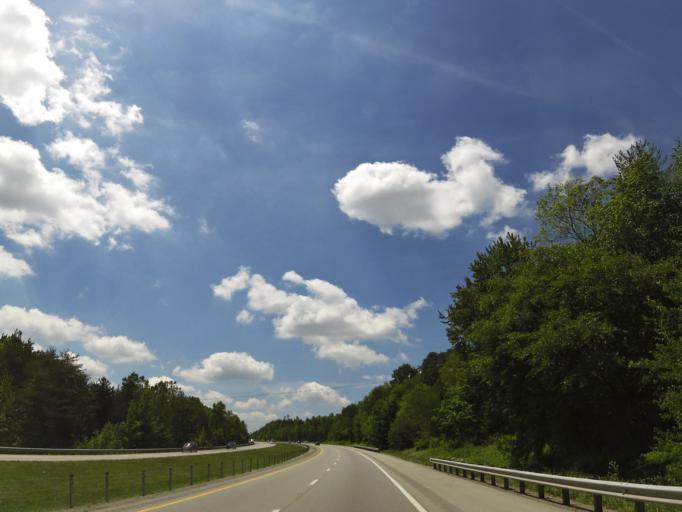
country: US
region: Kentucky
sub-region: Whitley County
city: Corbin
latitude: 36.8846
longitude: -84.1508
